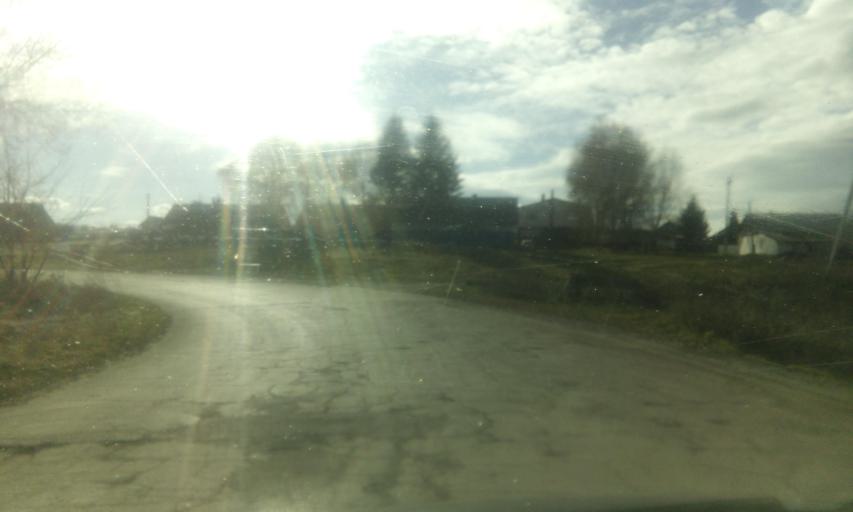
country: RU
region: Tula
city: Dubovka
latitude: 53.9473
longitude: 38.0277
